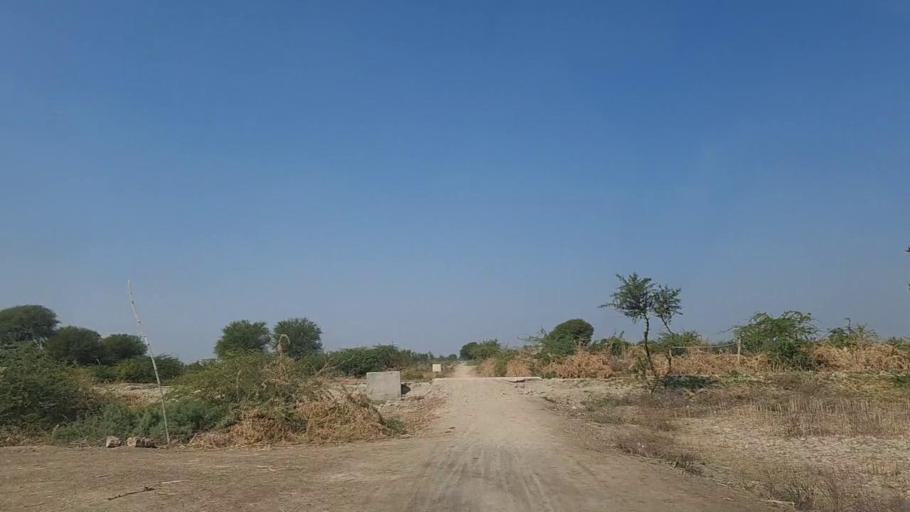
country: PK
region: Sindh
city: Digri
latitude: 25.2072
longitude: 69.1431
